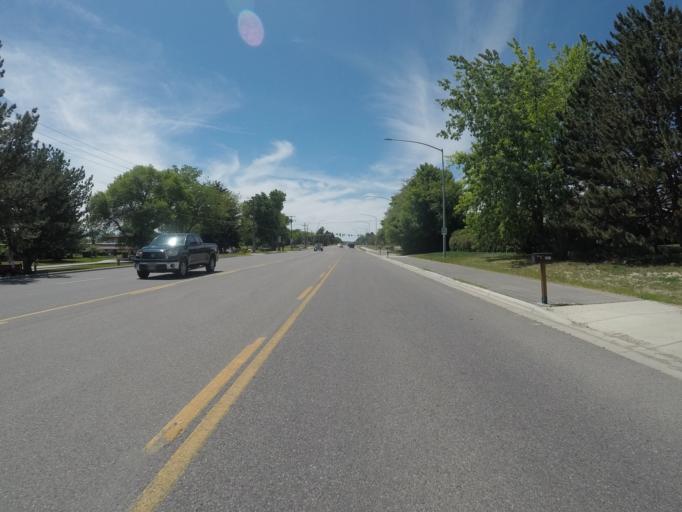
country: US
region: Montana
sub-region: Yellowstone County
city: Billings
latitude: 45.7986
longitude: -108.6152
